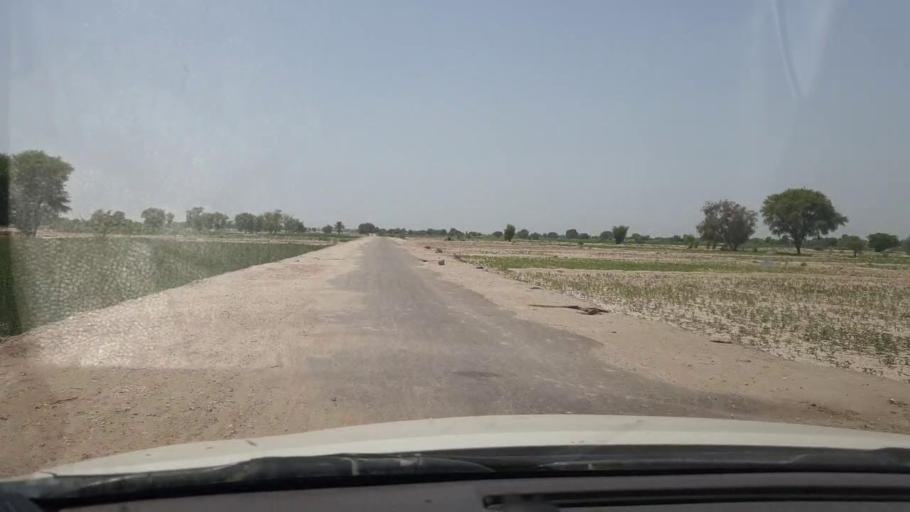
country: PK
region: Sindh
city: Rohri
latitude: 27.5207
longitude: 69.1782
